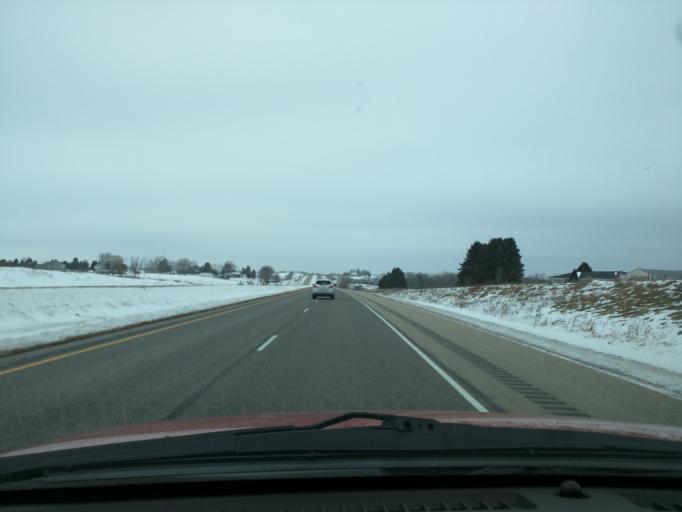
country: US
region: Minnesota
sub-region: Winona County
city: Winona
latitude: 43.9410
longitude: -91.6325
